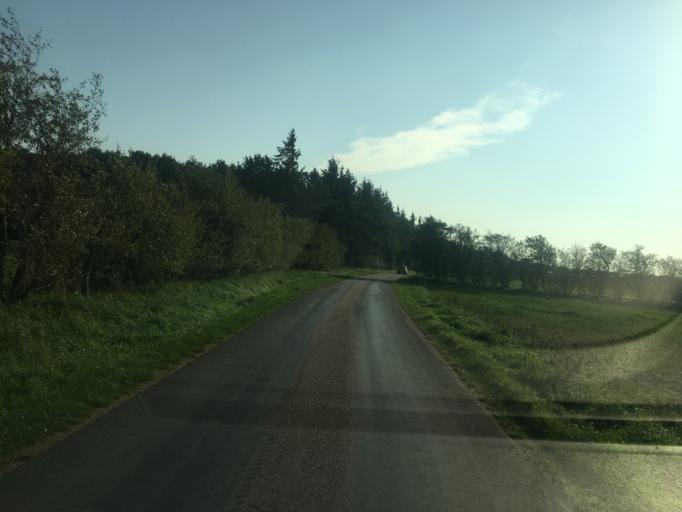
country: DE
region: Schleswig-Holstein
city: Bramstedtlund
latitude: 54.9261
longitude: 9.0579
